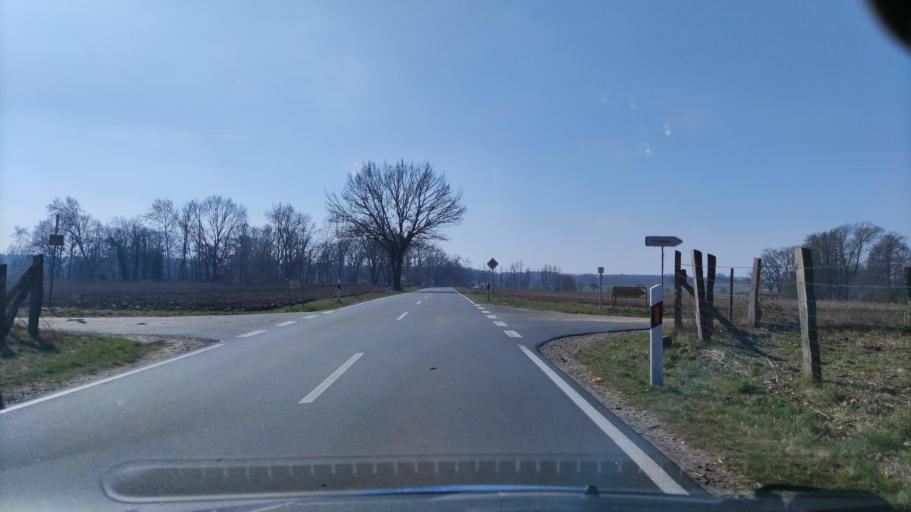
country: DE
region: Lower Saxony
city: Kusten
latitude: 52.9735
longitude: 11.0647
